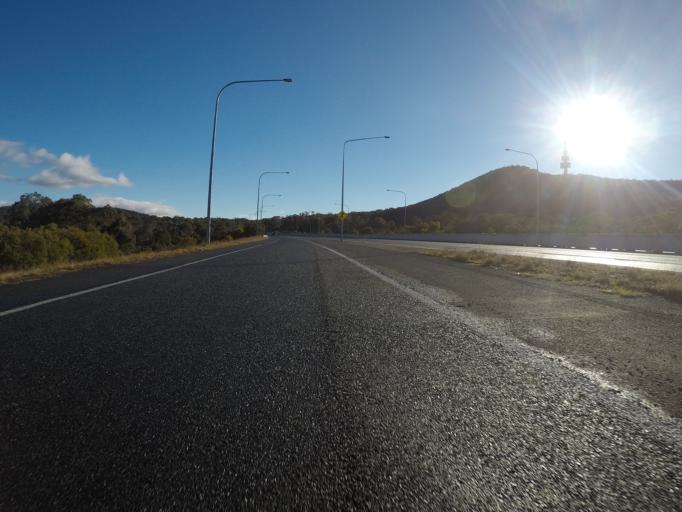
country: AU
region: Australian Capital Territory
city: Acton
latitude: -35.2826
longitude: 149.0858
